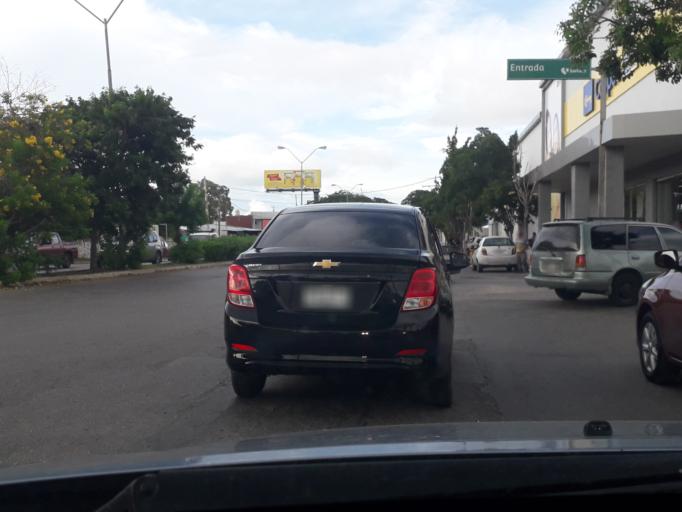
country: MX
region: Yucatan
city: Caucel
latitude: 20.9899
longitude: -89.6633
